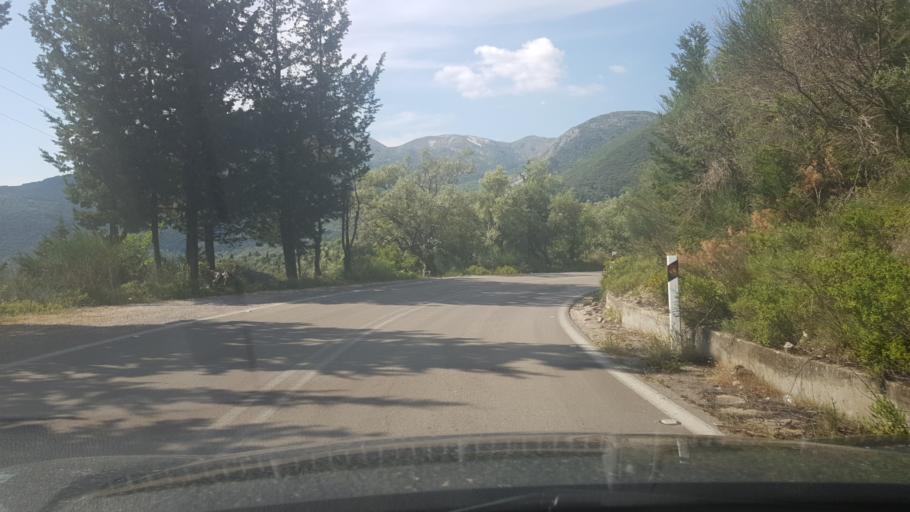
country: GR
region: Ionian Islands
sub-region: Lefkada
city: Nidri
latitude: 38.6560
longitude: 20.6569
